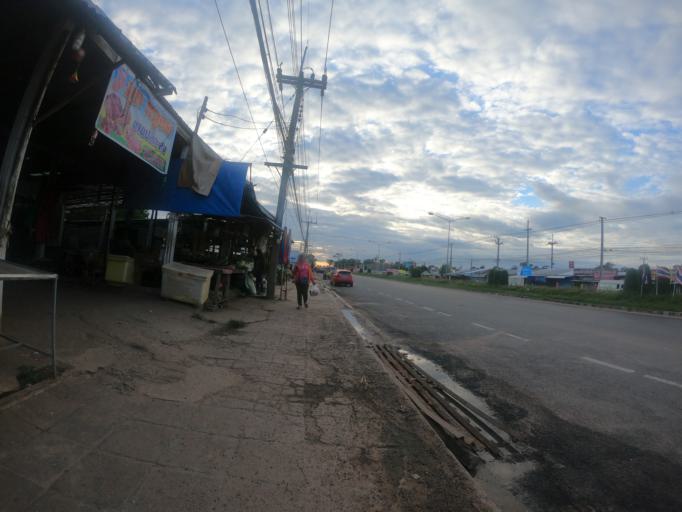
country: TH
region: Surin
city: Kap Choeng
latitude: 14.4531
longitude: 103.6904
